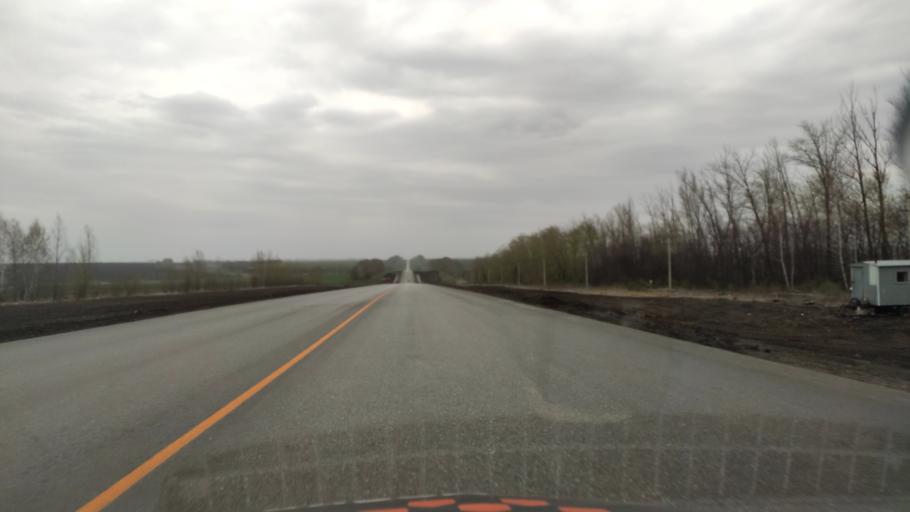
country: RU
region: Kursk
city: Gorshechnoye
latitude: 51.5480
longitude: 38.0948
